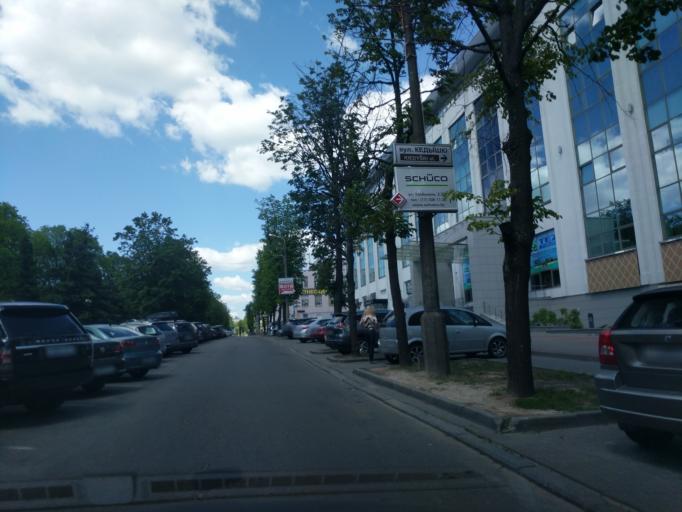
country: BY
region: Minsk
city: Minsk
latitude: 53.9256
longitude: 27.6146
